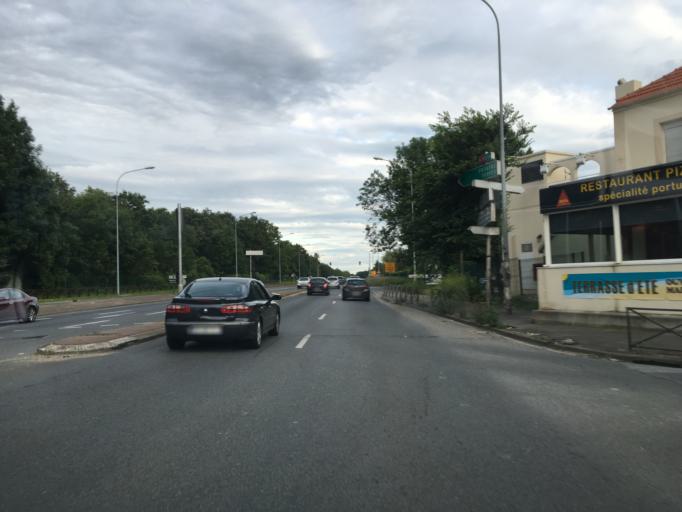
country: FR
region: Ile-de-France
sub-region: Departement du Val-de-Marne
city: Boissy-Saint-Leger
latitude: 48.7448
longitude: 2.5117
